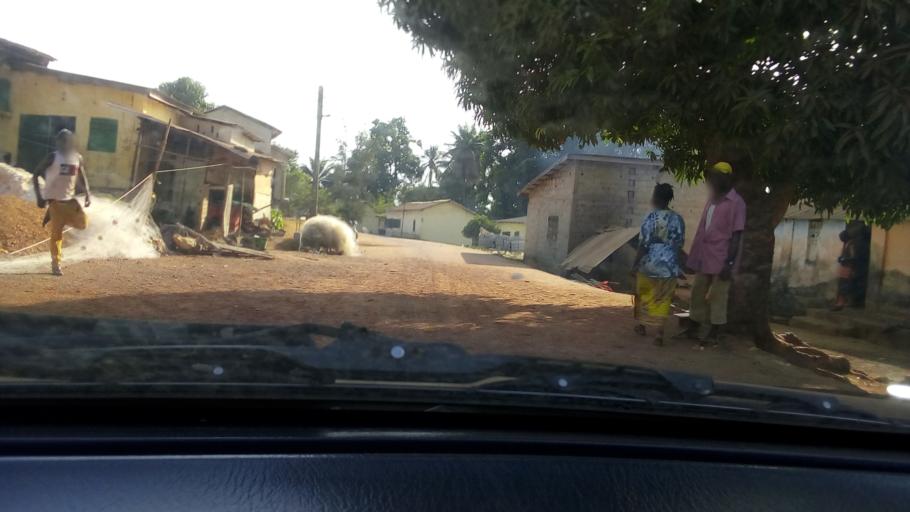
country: GN
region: Kindia
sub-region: Prefecture de Dubreka
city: Dubreka
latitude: 9.7912
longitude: -13.5270
